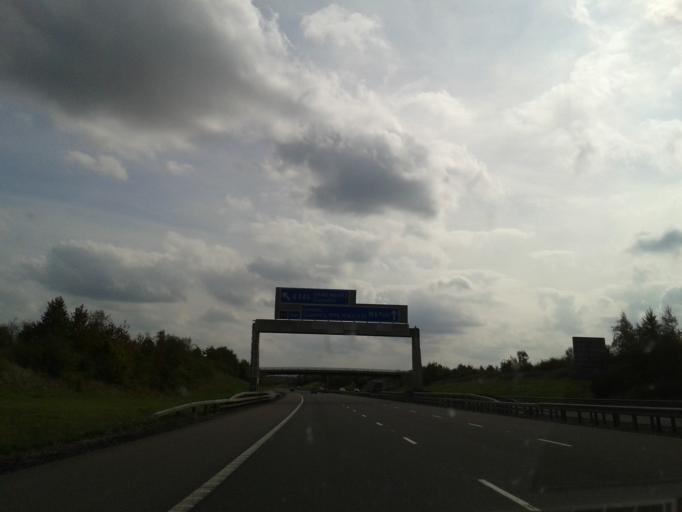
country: GB
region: England
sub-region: Warwickshire
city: Curdworth
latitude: 52.5577
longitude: -1.7485
